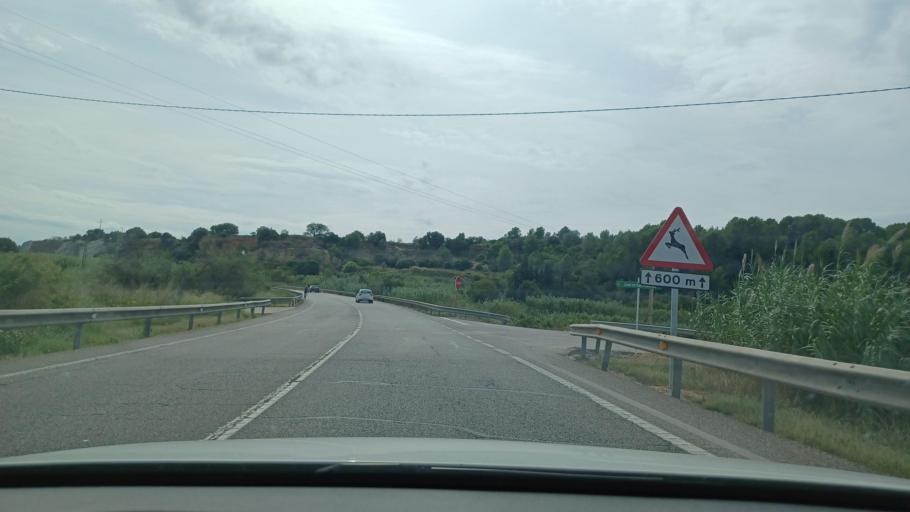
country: ES
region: Catalonia
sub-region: Provincia de Tarragona
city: Tortosa
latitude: 40.7897
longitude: 0.4961
